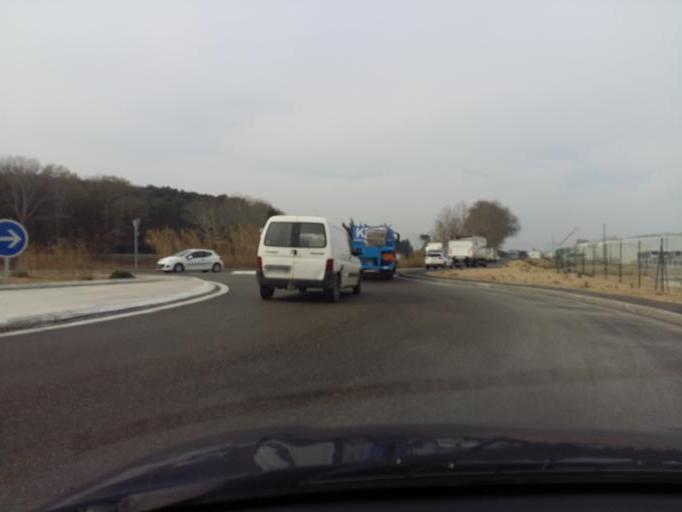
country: FR
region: Provence-Alpes-Cote d'Azur
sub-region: Departement des Bouches-du-Rhone
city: Noves
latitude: 43.8861
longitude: 4.8917
